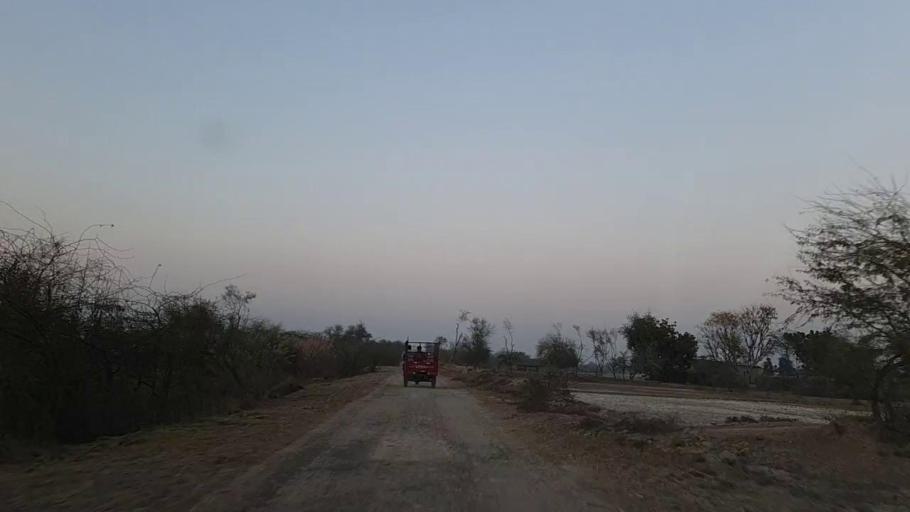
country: PK
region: Sindh
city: Bandhi
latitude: 26.6143
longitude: 68.3752
